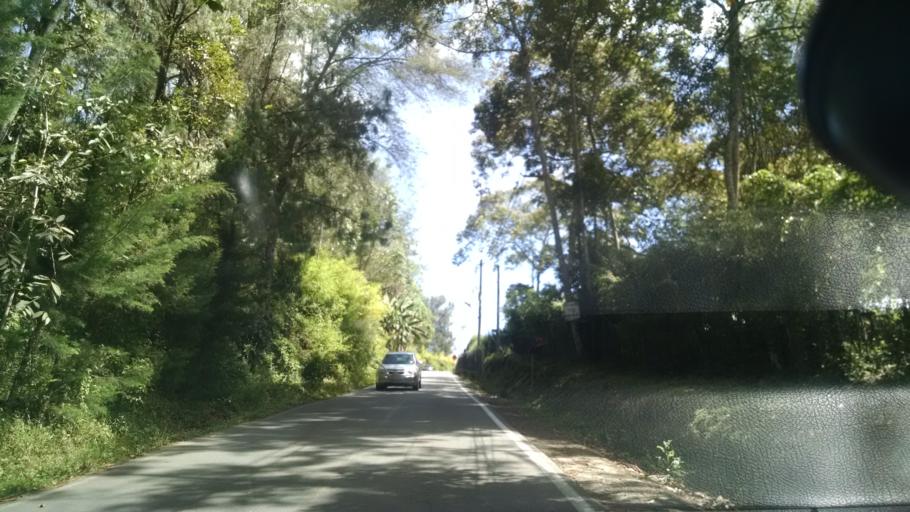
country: CO
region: Antioquia
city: El Retiro
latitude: 6.0829
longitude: -75.5015
